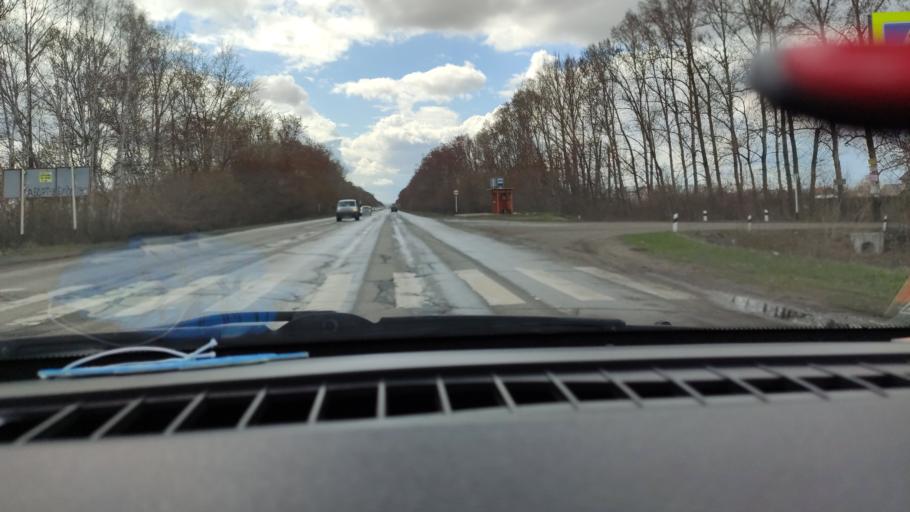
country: RU
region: Samara
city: Tol'yatti
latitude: 53.6269
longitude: 49.4163
